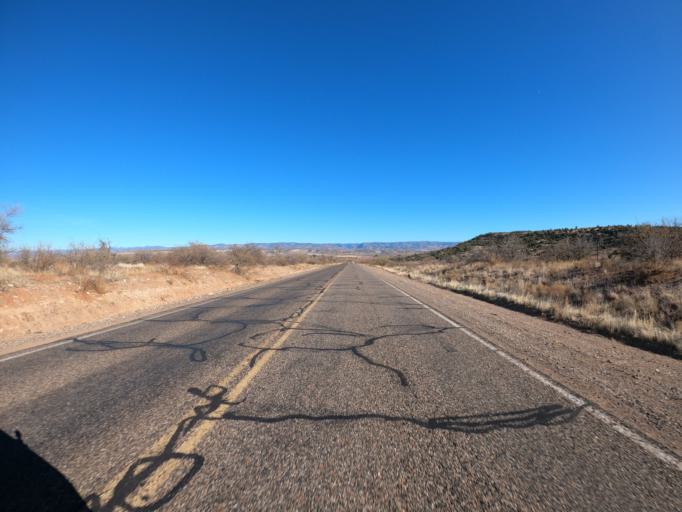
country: US
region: Arizona
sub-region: Yavapai County
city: Camp Verde
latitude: 34.5577
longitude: -111.8889
